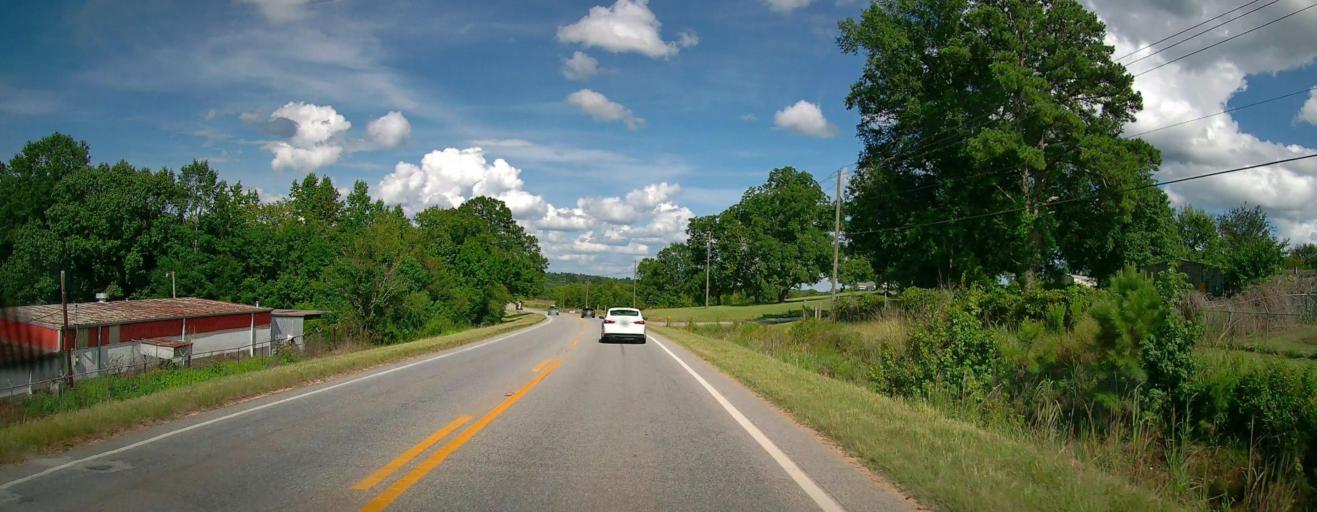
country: US
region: Alabama
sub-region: Russell County
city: Ladonia
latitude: 32.4602
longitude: -85.1457
